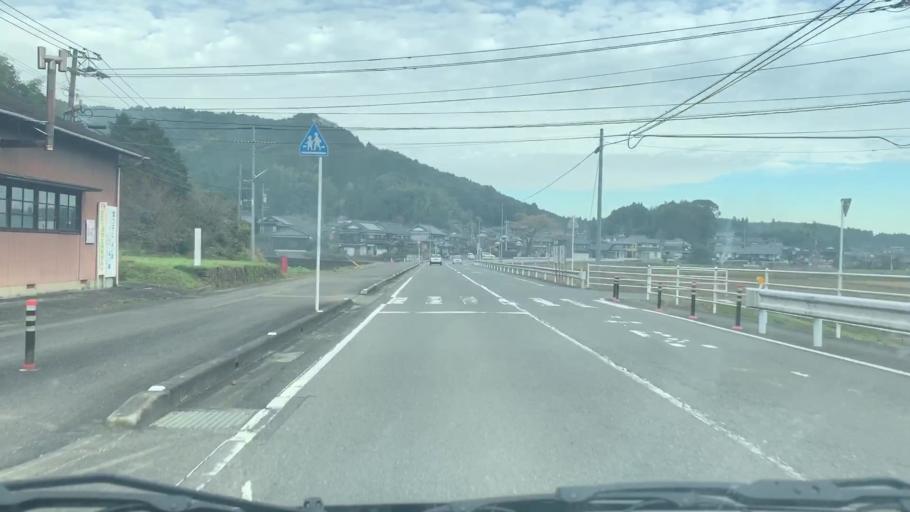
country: JP
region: Saga Prefecture
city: Takeocho-takeo
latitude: 33.1985
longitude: 129.9614
